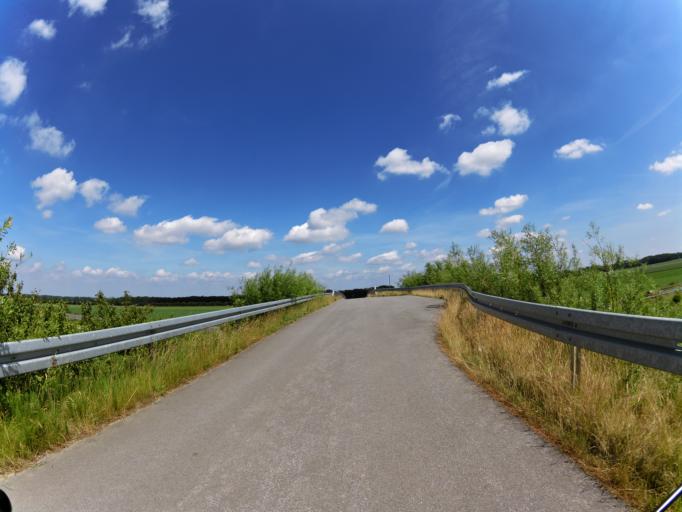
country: DE
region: North Rhine-Westphalia
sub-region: Regierungsbezirk Koln
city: Selfkant
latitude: 51.0273
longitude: 5.8962
